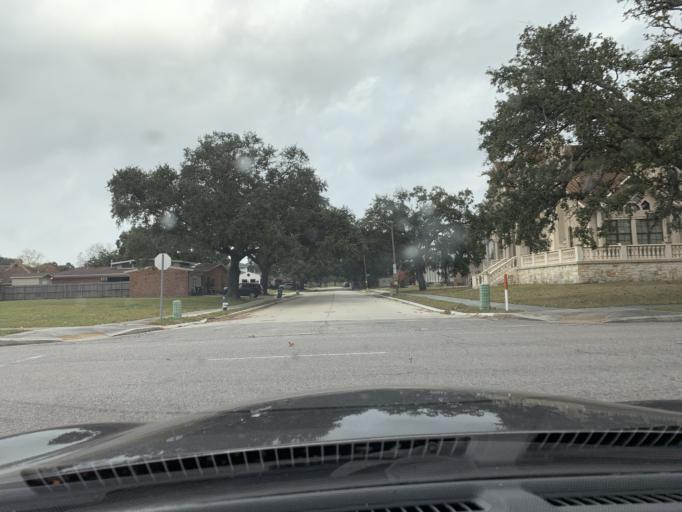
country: US
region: Louisiana
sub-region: Jefferson Parish
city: Metairie
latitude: 30.0189
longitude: -90.0998
